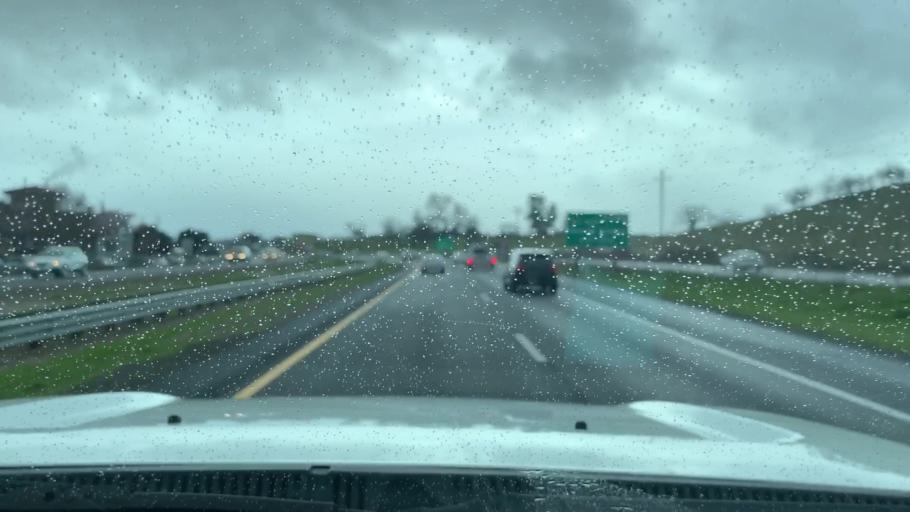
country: US
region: California
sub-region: San Luis Obispo County
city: Paso Robles
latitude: 35.5977
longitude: -120.6926
